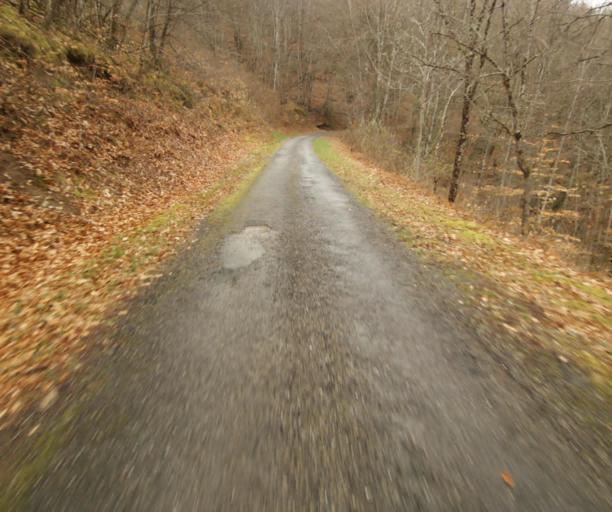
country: FR
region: Limousin
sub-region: Departement de la Correze
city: Saint-Privat
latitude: 45.2154
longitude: 2.0331
